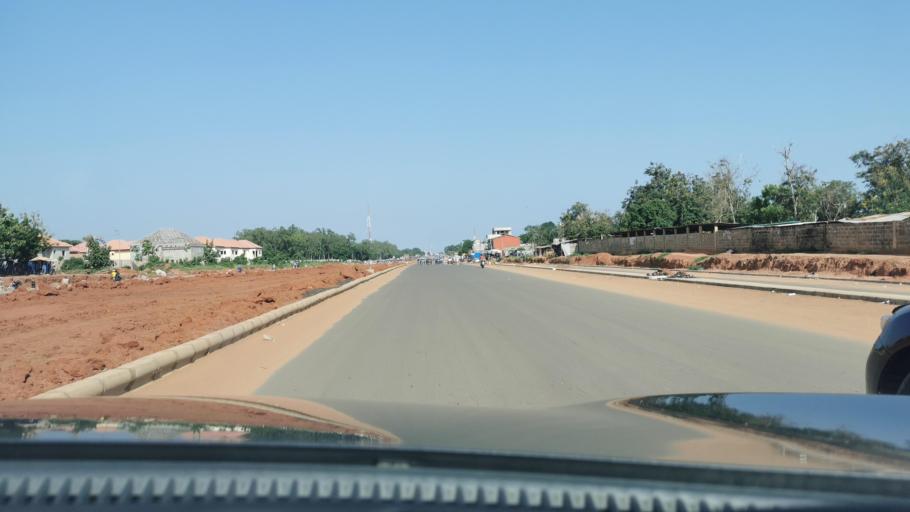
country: TG
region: Maritime
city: Lome
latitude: 6.1937
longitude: 1.1568
